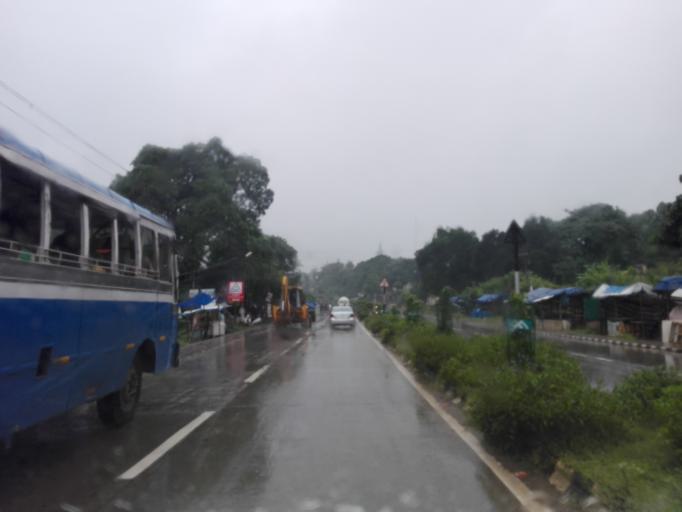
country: IN
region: Kerala
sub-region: Ernakulam
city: Elur
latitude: 10.0530
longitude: 76.3319
